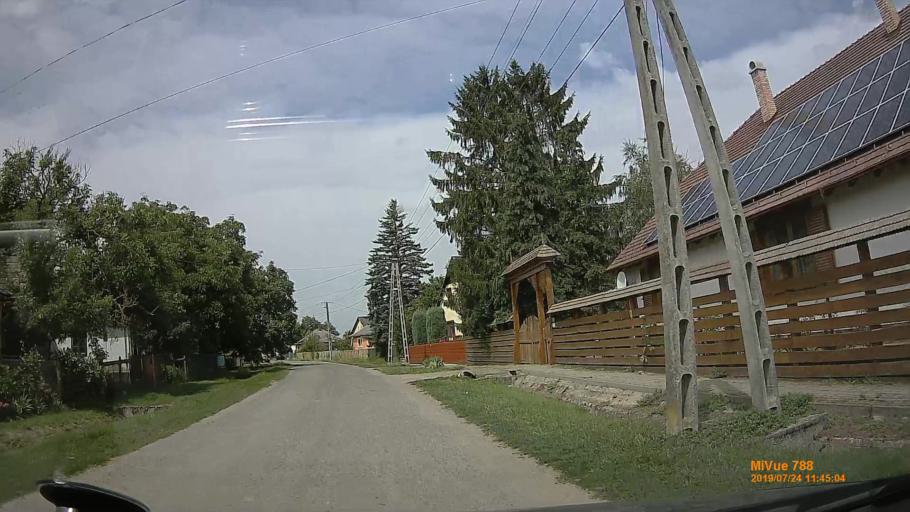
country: UA
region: Zakarpattia
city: Batiovo
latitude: 48.2318
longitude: 22.4363
